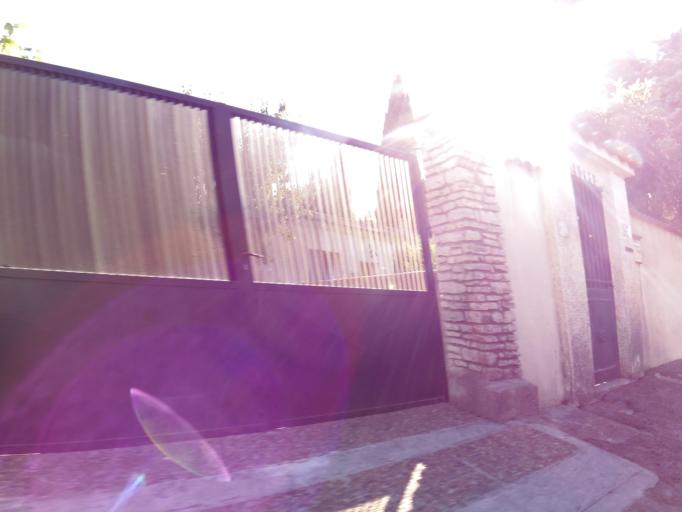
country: FR
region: Languedoc-Roussillon
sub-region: Departement du Gard
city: Nimes
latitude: 43.8489
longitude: 4.3605
